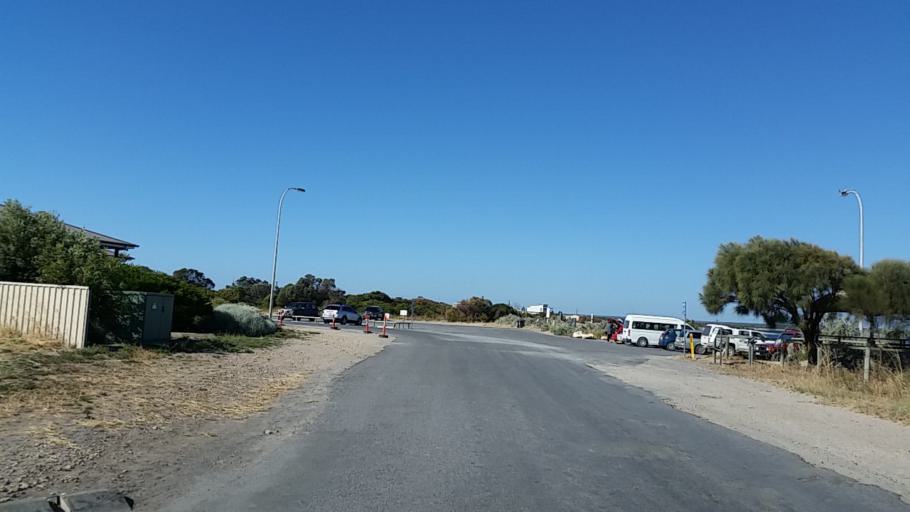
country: AU
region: South Australia
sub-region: Yorke Peninsula
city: Honiton
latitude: -35.2369
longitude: 136.9815
